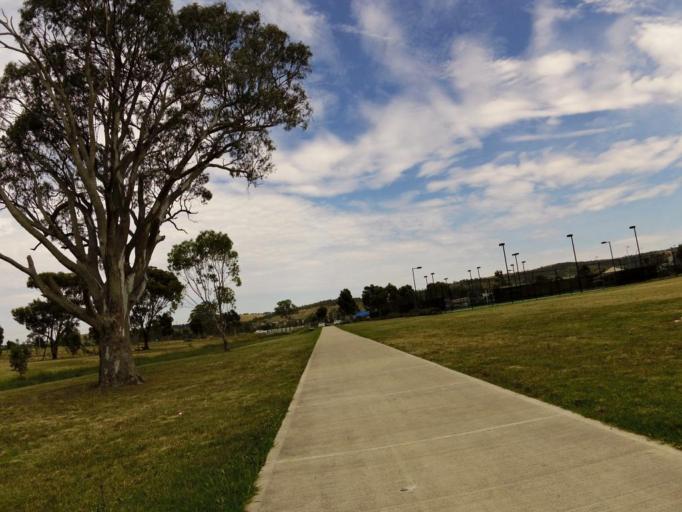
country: AU
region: Victoria
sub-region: Whittlesea
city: Mernda
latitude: -37.6311
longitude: 145.0802
